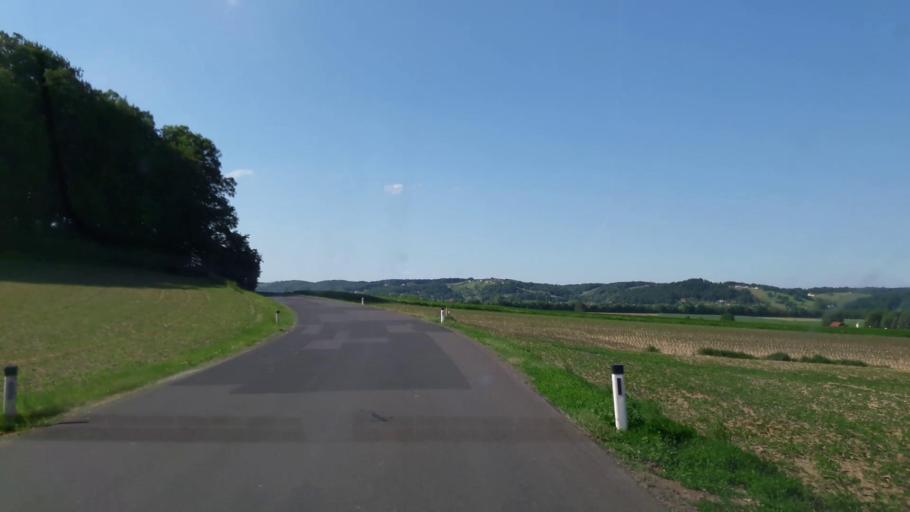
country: AT
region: Styria
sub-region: Politischer Bezirk Suedoststeiermark
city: Fehring
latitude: 46.9320
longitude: 16.0323
